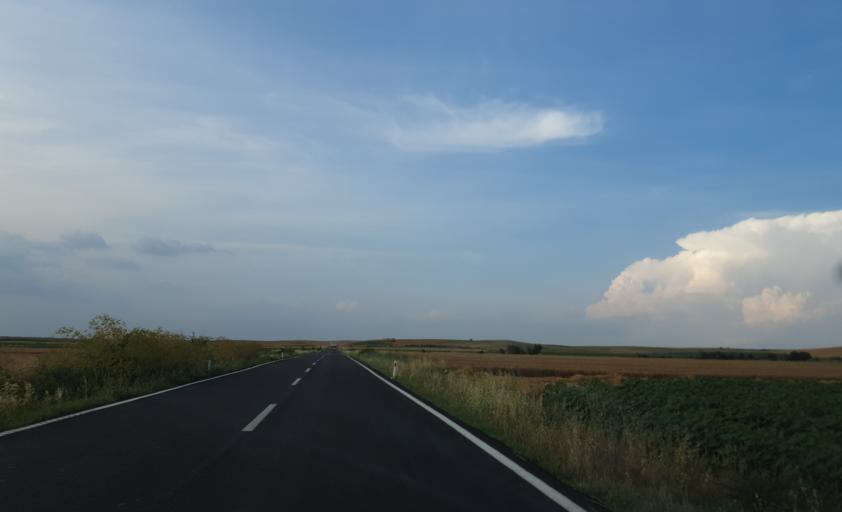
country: TR
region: Tekirdag
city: Hayrabolu
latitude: 41.2448
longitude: 27.1351
